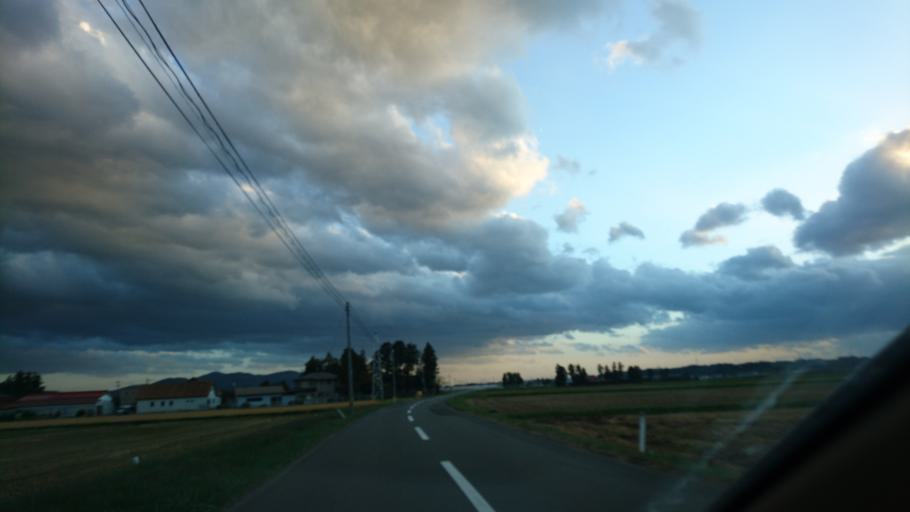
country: JP
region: Iwate
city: Mizusawa
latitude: 39.1106
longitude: 141.1503
